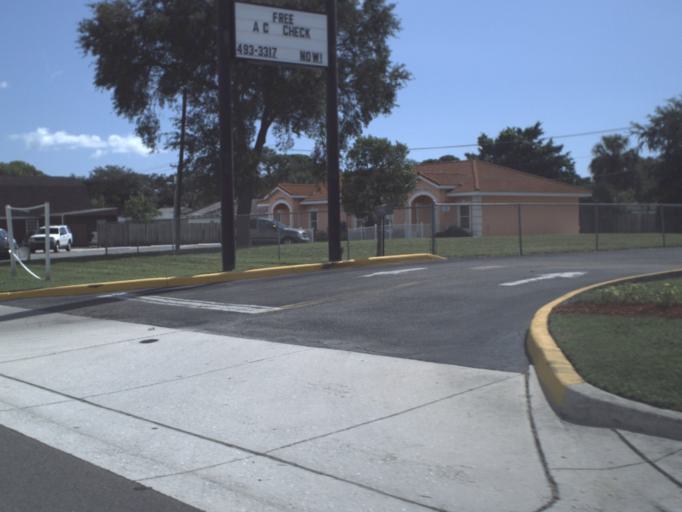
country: US
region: Florida
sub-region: Sarasota County
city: Venice Gardens
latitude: 27.0665
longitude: -82.4198
